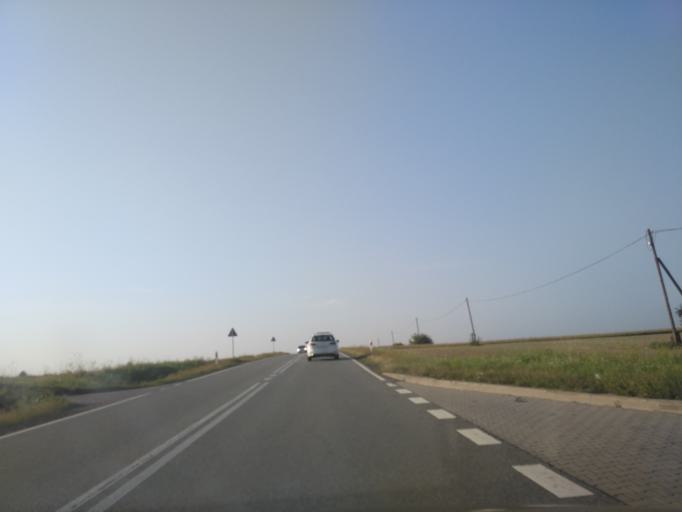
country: PL
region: Lublin Voivodeship
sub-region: Powiat janowski
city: Modliborzyce
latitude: 50.7799
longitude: 22.3237
